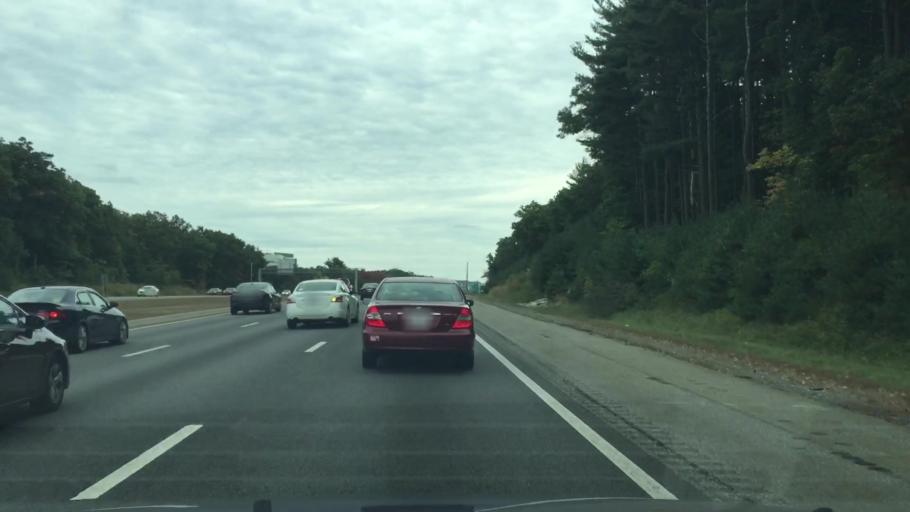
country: US
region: Massachusetts
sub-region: Middlesex County
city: Burlington
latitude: 42.4871
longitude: -71.2286
